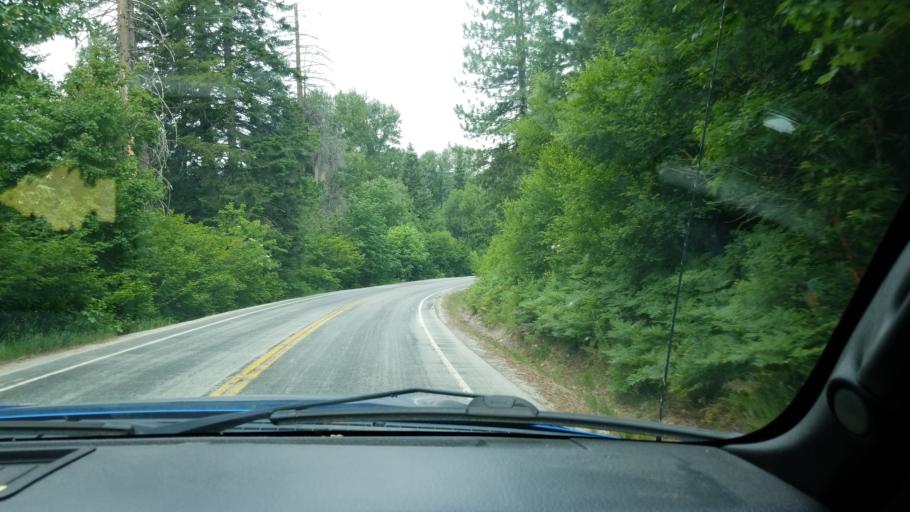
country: US
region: Washington
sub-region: Chelan County
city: Leavenworth
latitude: 47.8471
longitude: -120.8264
